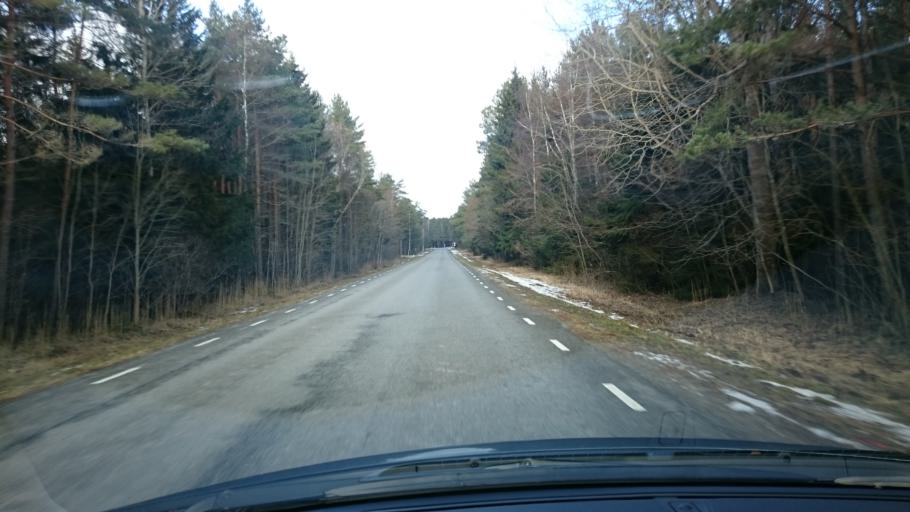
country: EE
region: Harju
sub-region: Keila linn
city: Keila
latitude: 59.3889
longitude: 24.2960
